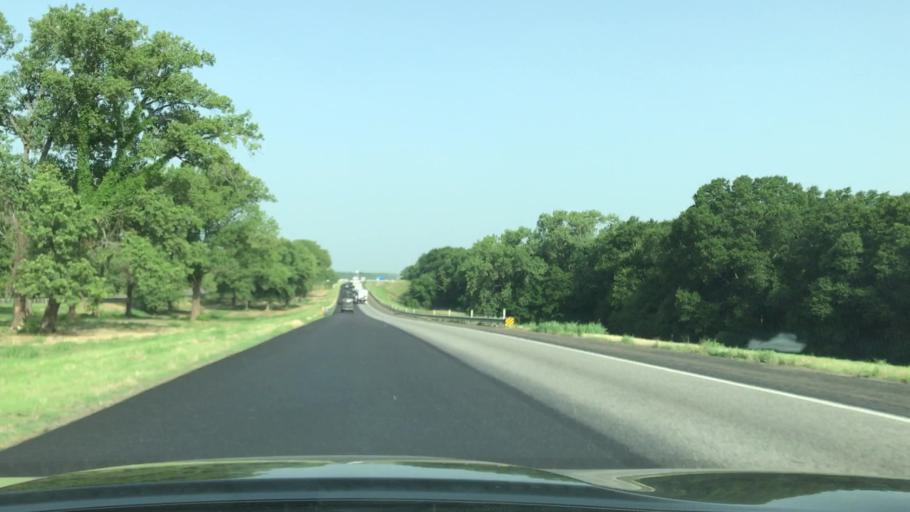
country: US
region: Texas
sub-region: Van Zandt County
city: Wills Point
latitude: 32.6656
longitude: -96.1315
